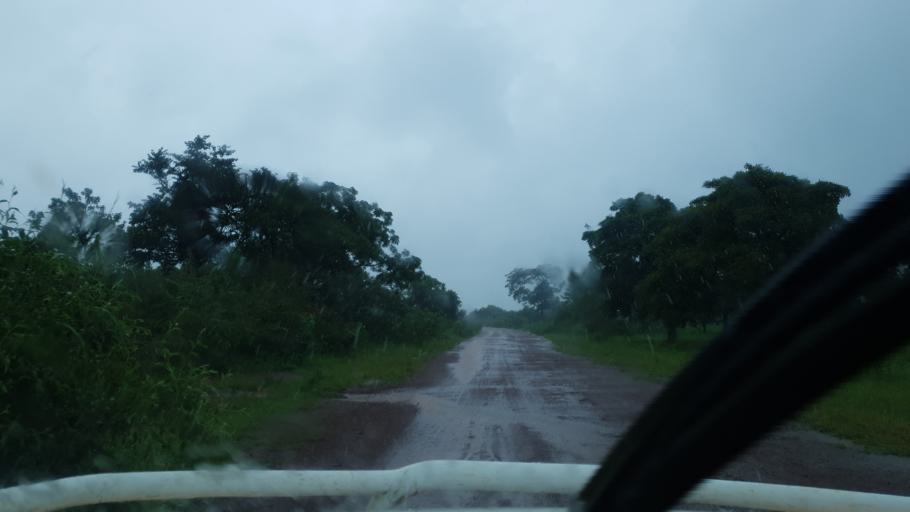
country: ML
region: Sikasso
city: Kolondieba
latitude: 11.6082
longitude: -6.6752
